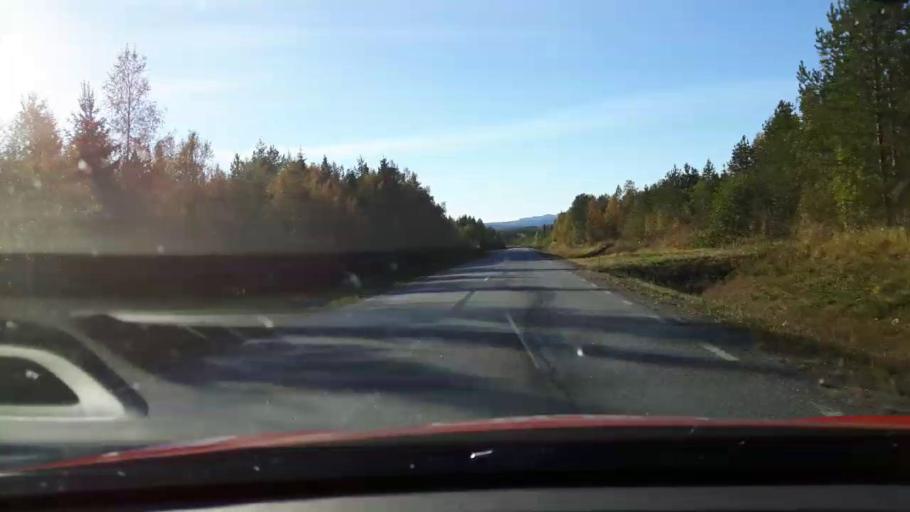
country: SE
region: Jaemtland
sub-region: OEstersunds Kommun
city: Lit
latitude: 63.8586
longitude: 14.9839
